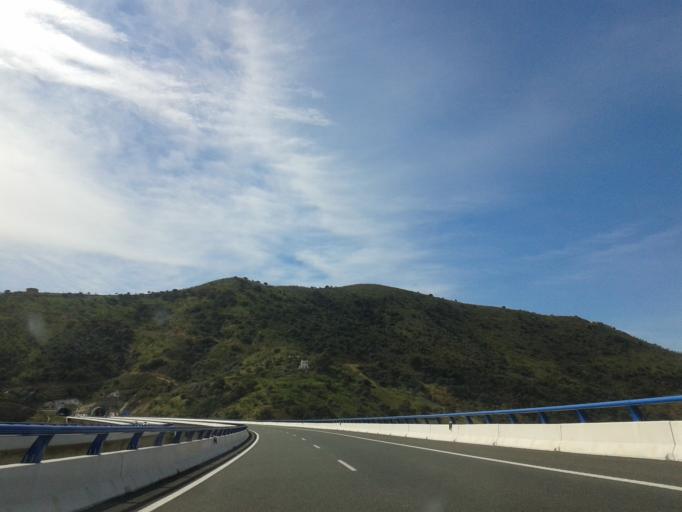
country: ES
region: Andalusia
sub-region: Provincia de Malaga
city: Casabermeja
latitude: 36.8766
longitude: -4.4815
